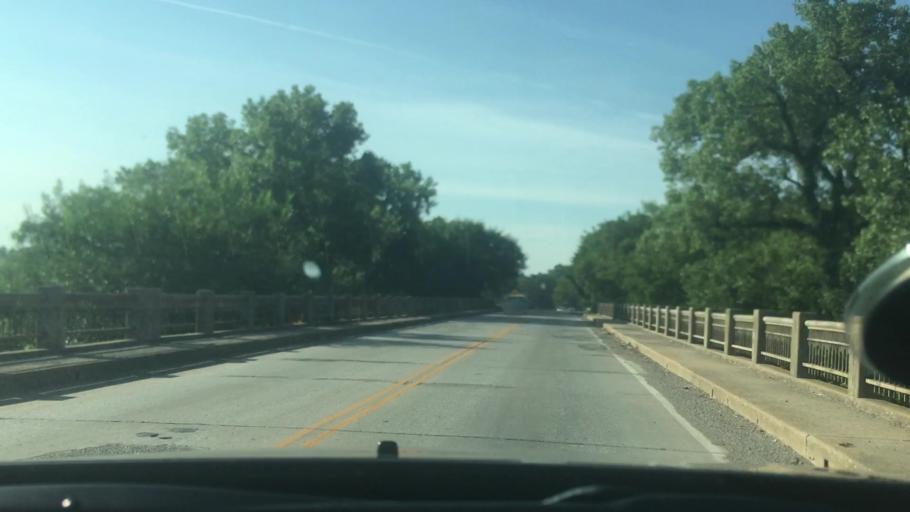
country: US
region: Oklahoma
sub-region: Garvin County
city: Pauls Valley
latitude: 34.7346
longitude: -97.2141
